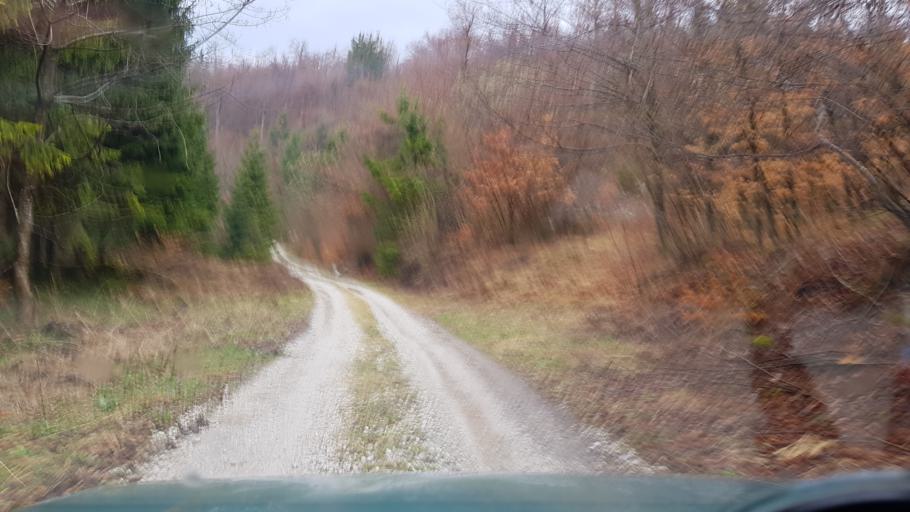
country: SI
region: Cerkno
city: Cerkno
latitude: 46.1329
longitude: 13.8646
